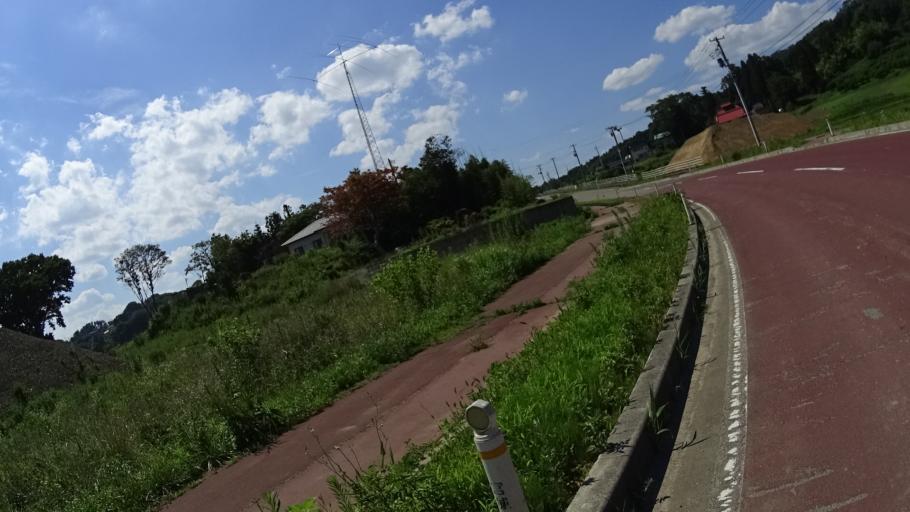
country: JP
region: Iwate
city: Ofunato
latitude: 38.8628
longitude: 141.6215
